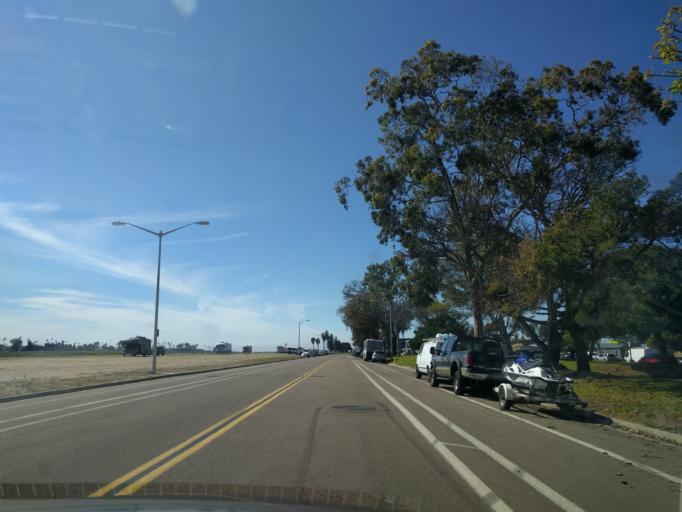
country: US
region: California
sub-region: San Diego County
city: San Diego
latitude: 32.7591
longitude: -117.2365
